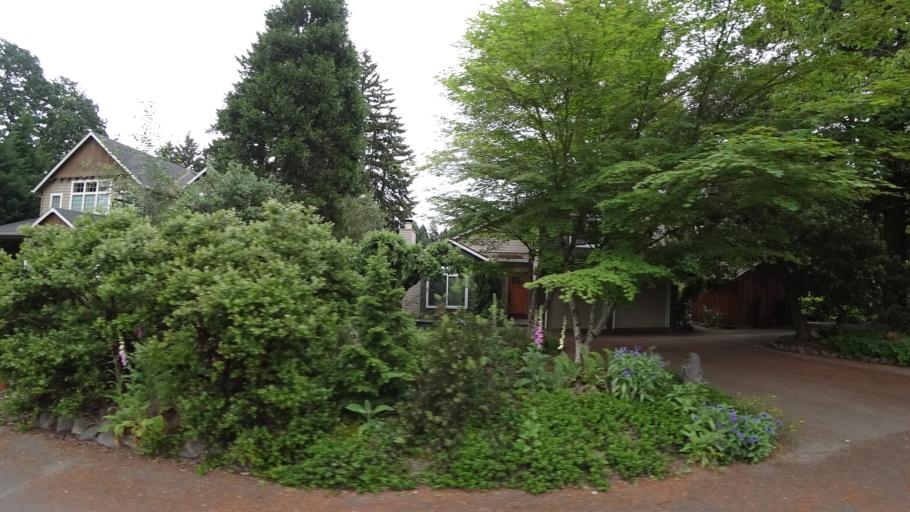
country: US
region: Oregon
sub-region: Washington County
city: Garden Home-Whitford
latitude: 45.4662
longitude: -122.7343
